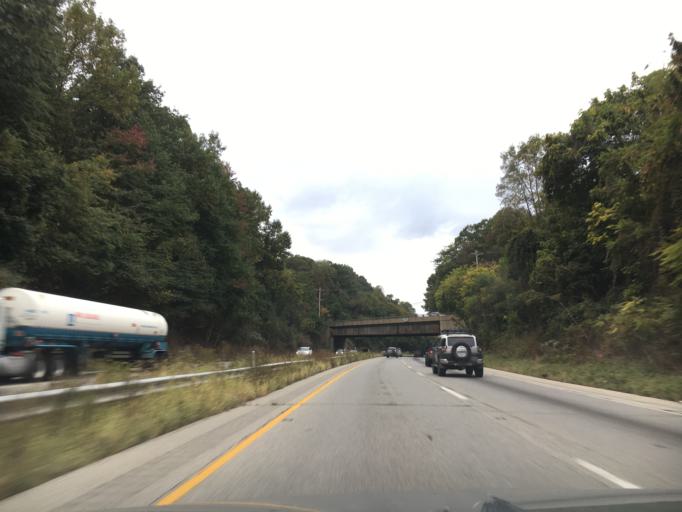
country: US
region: Pennsylvania
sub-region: Chester County
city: Caln
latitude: 40.0045
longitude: -75.7769
